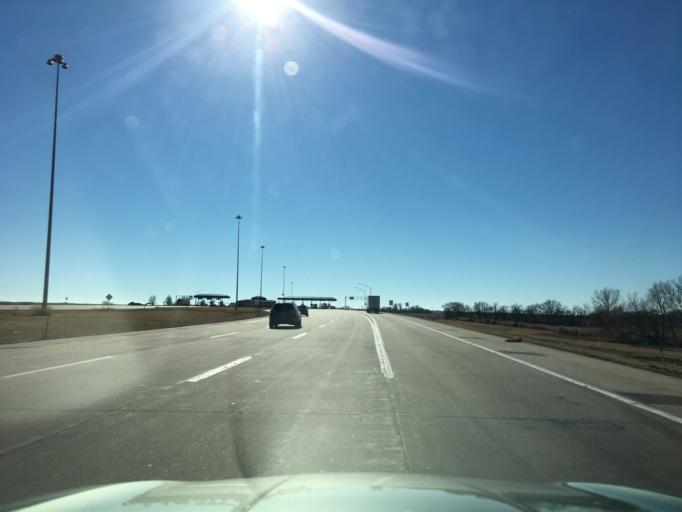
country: US
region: Kansas
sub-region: Sumner County
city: Wellington
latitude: 37.2426
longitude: -97.3392
